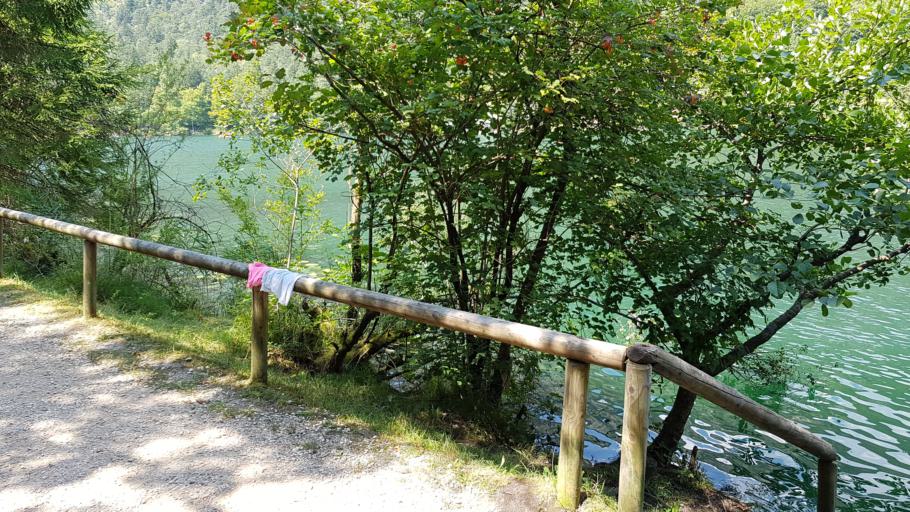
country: DE
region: Bavaria
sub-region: Upper Bavaria
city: Schneizlreuth
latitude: 47.7181
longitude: 12.8248
